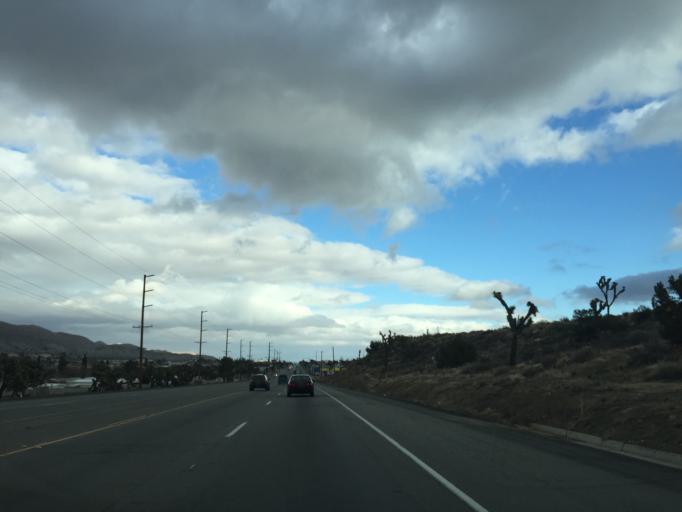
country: US
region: California
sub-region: San Bernardino County
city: Yucca Valley
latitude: 34.1145
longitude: -116.4646
